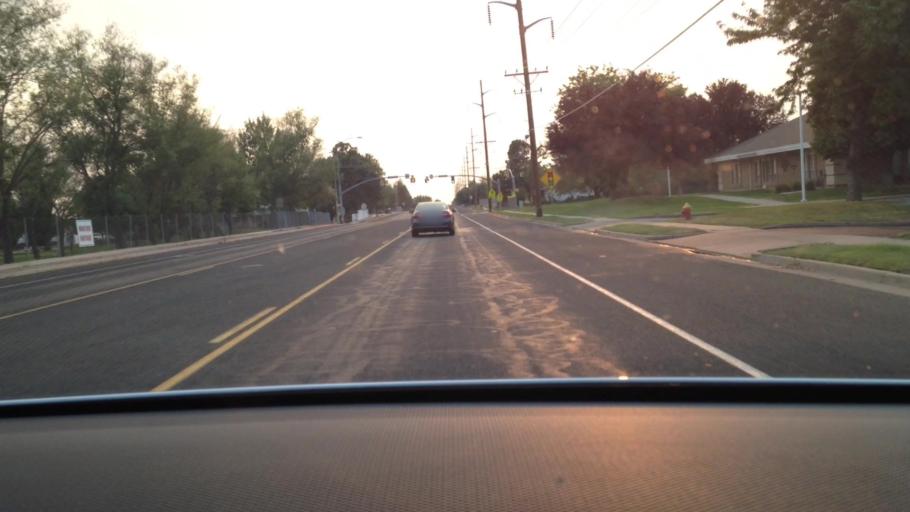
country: US
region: Utah
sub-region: Davis County
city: Layton
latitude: 41.0747
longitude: -112.0052
